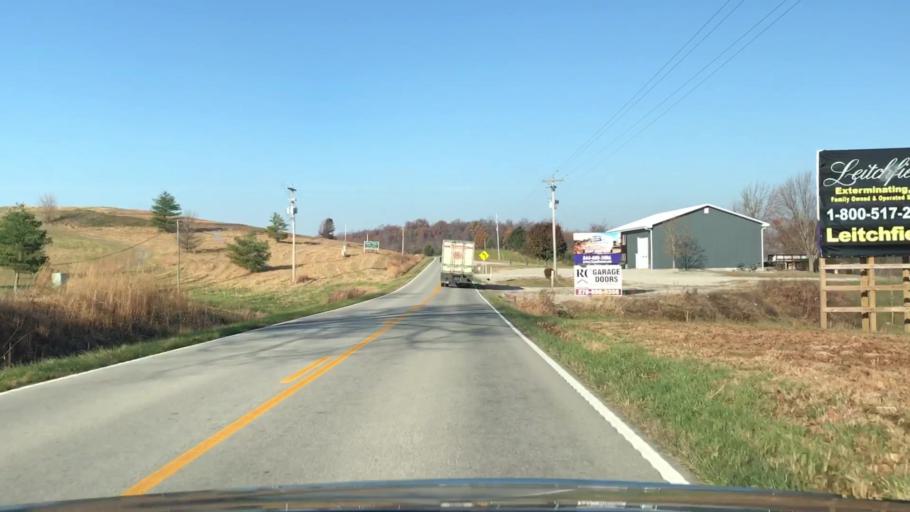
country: US
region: Kentucky
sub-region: Grayson County
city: Leitchfield
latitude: 37.4077
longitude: -86.2550
